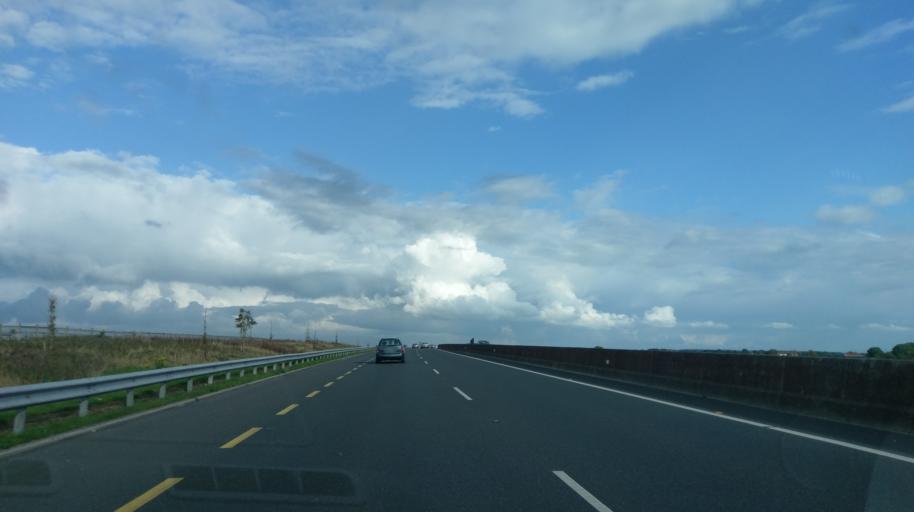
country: IE
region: Connaught
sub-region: County Galway
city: Oranmore
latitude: 53.2925
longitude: -8.9591
